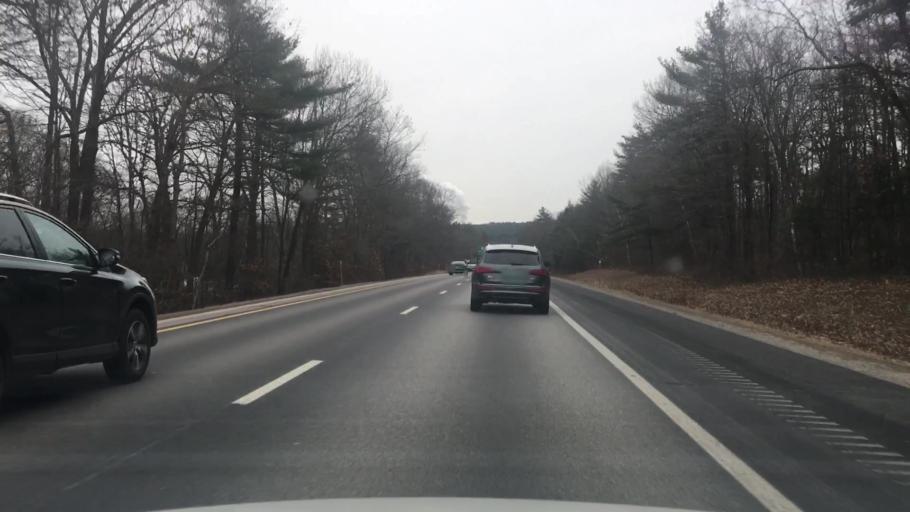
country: US
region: New Hampshire
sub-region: Merrimack County
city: Concord
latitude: 43.1725
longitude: -71.5509
